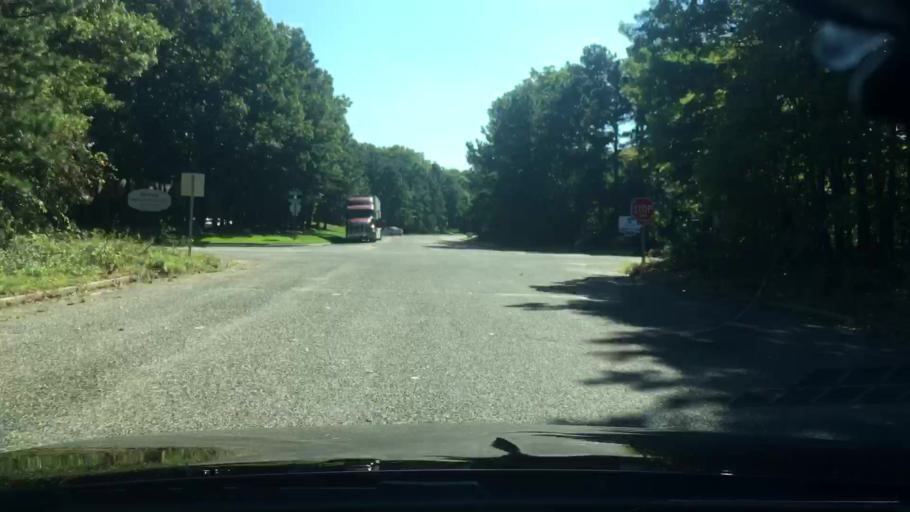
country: US
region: New York
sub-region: Suffolk County
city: Yaphank
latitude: 40.8472
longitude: -72.8804
